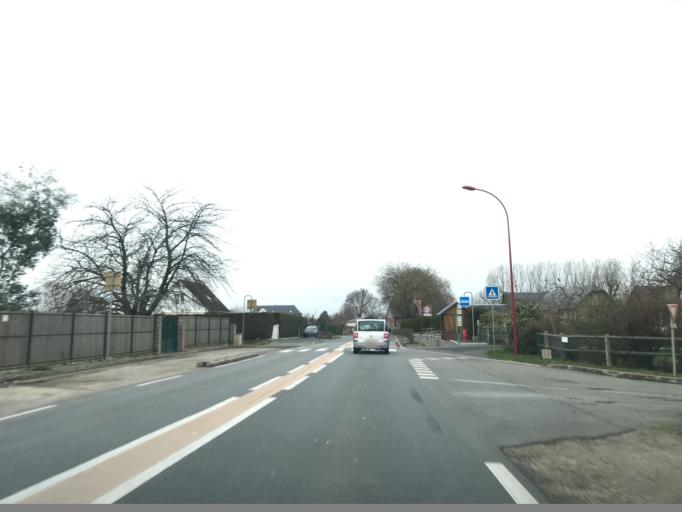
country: FR
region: Haute-Normandie
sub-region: Departement de l'Eure
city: Fleury-sur-Andelle
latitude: 49.3839
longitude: 1.3151
